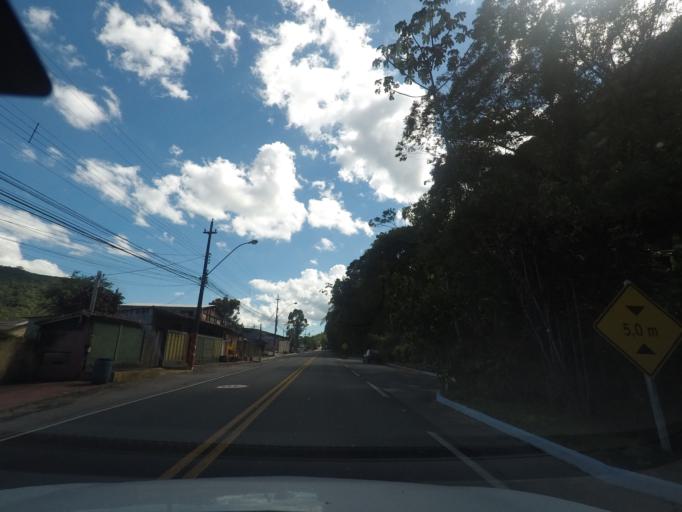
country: BR
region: Rio de Janeiro
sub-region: Teresopolis
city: Teresopolis
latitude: -22.4536
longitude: -42.9831
